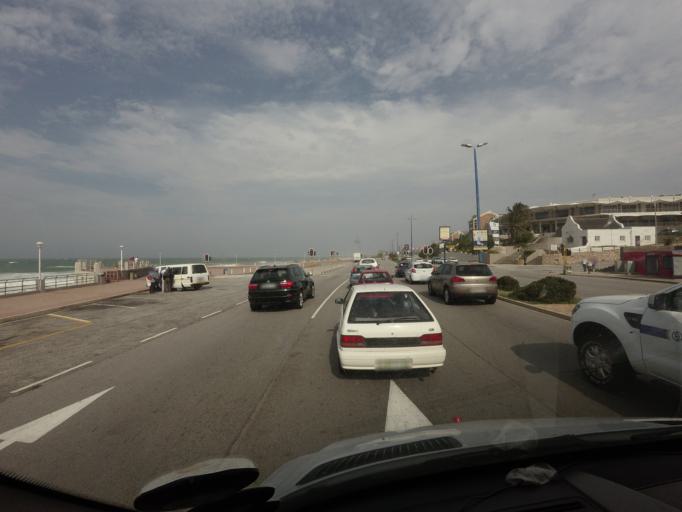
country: ZA
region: Eastern Cape
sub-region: Nelson Mandela Bay Metropolitan Municipality
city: Port Elizabeth
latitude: -33.9768
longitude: 25.6496
